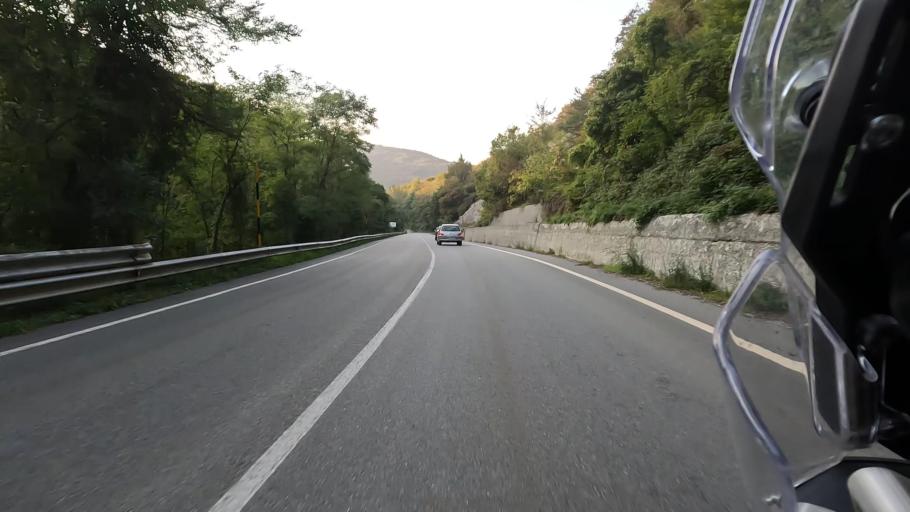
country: IT
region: Liguria
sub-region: Provincia di Savona
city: Osteria dei Cacciatori-Stella
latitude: 44.4438
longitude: 8.4841
